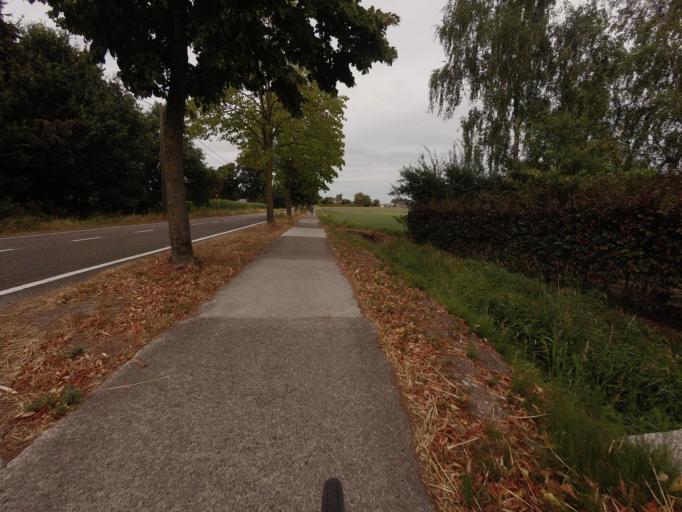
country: BE
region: Flanders
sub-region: Provincie Antwerpen
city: Brecht
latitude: 51.3321
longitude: 4.6320
